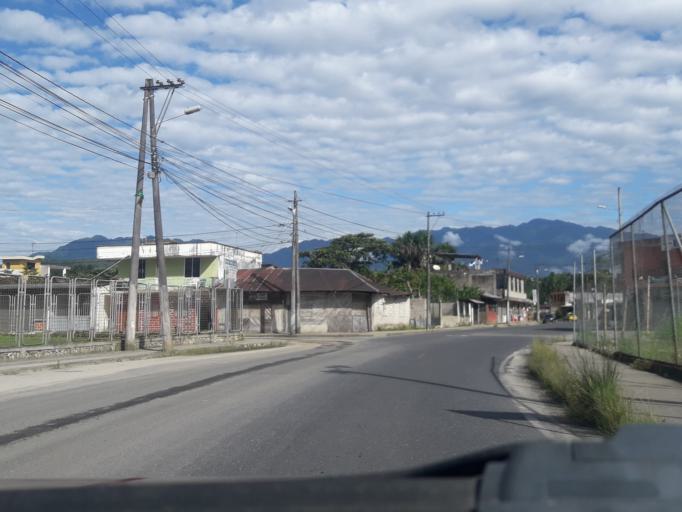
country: EC
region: Napo
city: Tena
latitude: -0.9867
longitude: -77.8293
